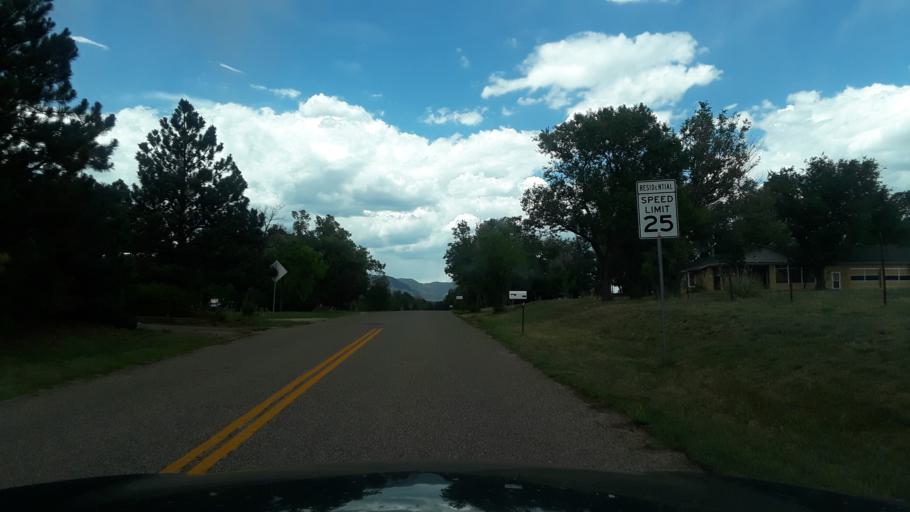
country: US
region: Colorado
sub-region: El Paso County
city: Air Force Academy
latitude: 38.9406
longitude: -104.8140
